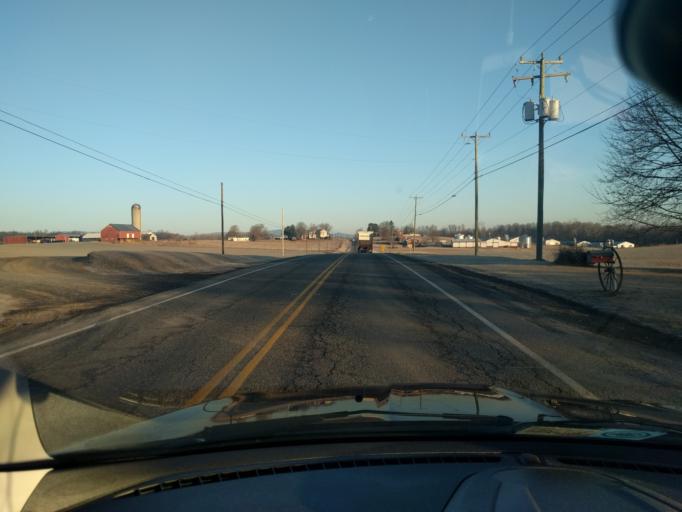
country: US
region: Virginia
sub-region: Augusta County
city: Weyers Cave
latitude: 38.3375
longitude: -78.9392
